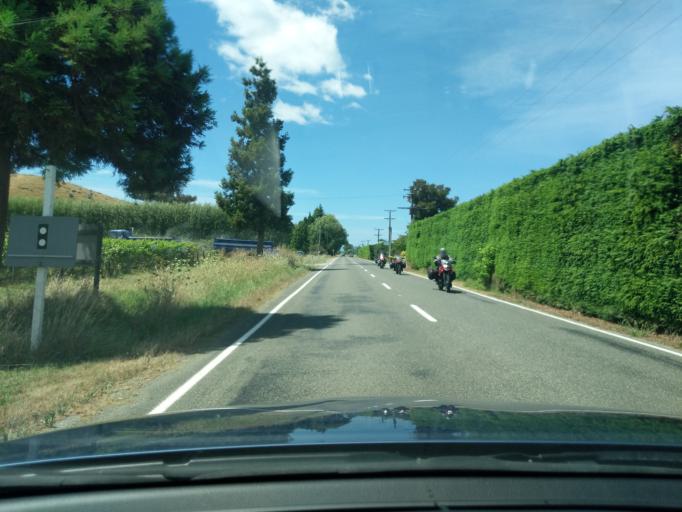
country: NZ
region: Tasman
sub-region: Tasman District
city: Motueka
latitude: -41.0628
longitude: 172.9791
